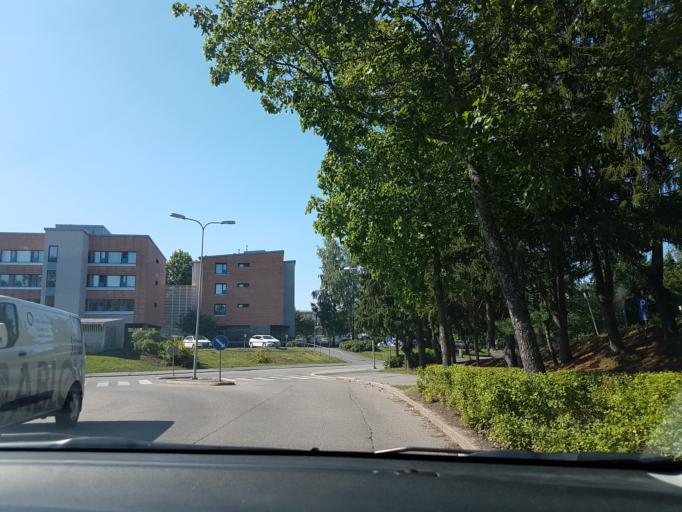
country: FI
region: Uusimaa
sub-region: Helsinki
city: Vantaa
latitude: 60.2460
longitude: 24.9852
